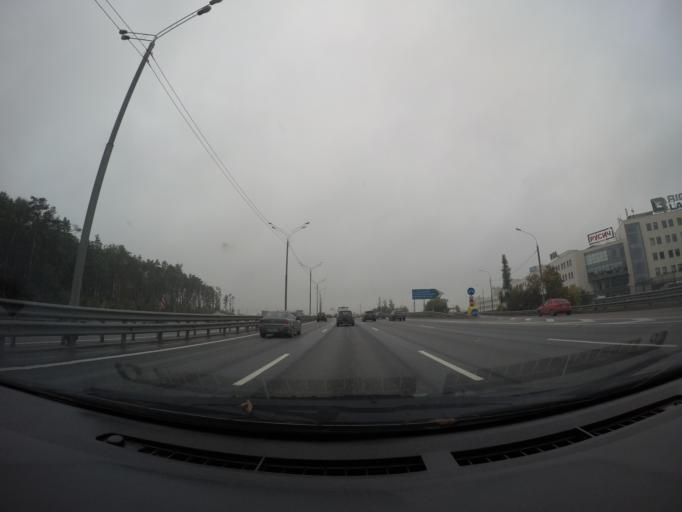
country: RU
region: Moskovskaya
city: Opalikha
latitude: 55.7847
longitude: 37.2449
